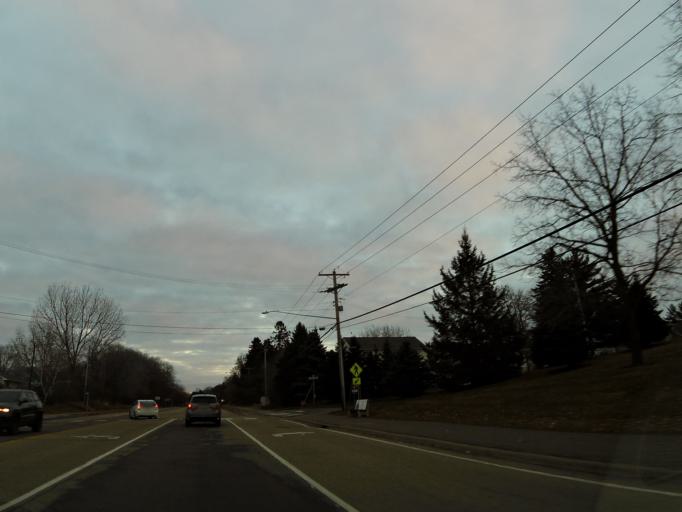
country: US
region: Minnesota
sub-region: Washington County
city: Birchwood
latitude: 45.0502
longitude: -92.9785
